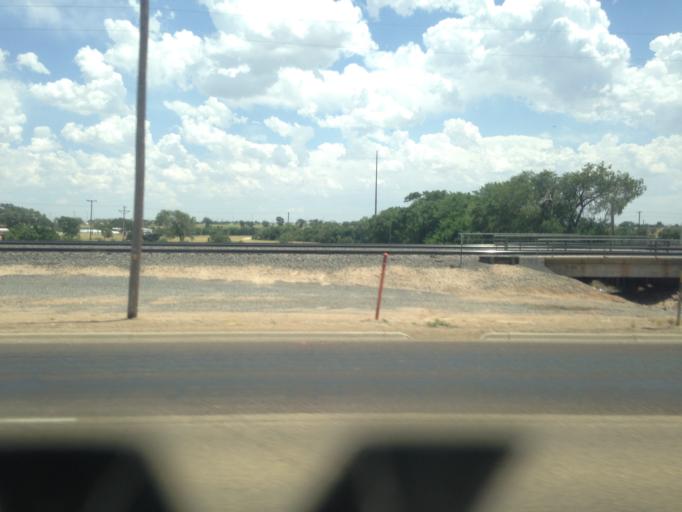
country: US
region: Texas
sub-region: Deaf Smith County
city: Hereford
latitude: 34.8211
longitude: -102.3856
